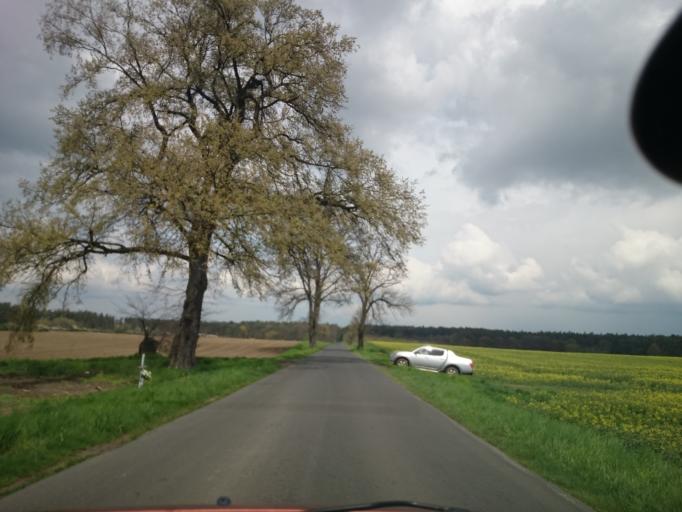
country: PL
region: Opole Voivodeship
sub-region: Powiat strzelecki
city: Izbicko
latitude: 50.5314
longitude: 18.1314
